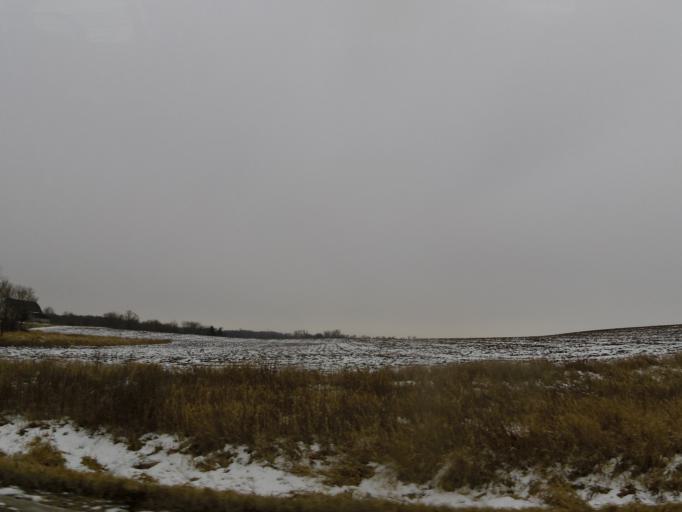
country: US
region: Minnesota
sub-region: Scott County
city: Prior Lake
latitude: 44.6305
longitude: -93.4856
